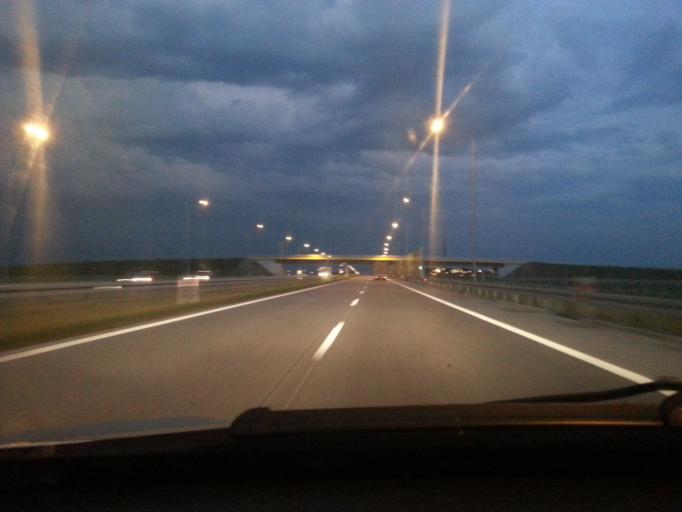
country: PL
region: Lodz Voivodeship
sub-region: Powiat sieradzki
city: Sieradz
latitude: 51.5343
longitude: 18.6962
